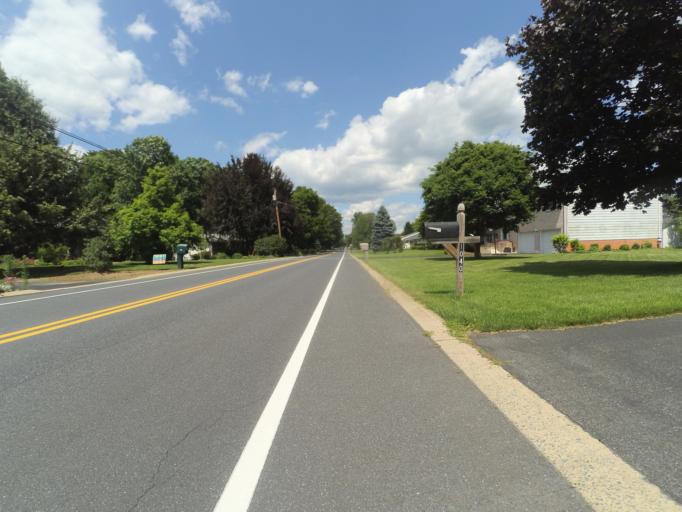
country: US
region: Pennsylvania
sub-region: Centre County
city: Lemont
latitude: 40.8025
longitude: -77.8341
